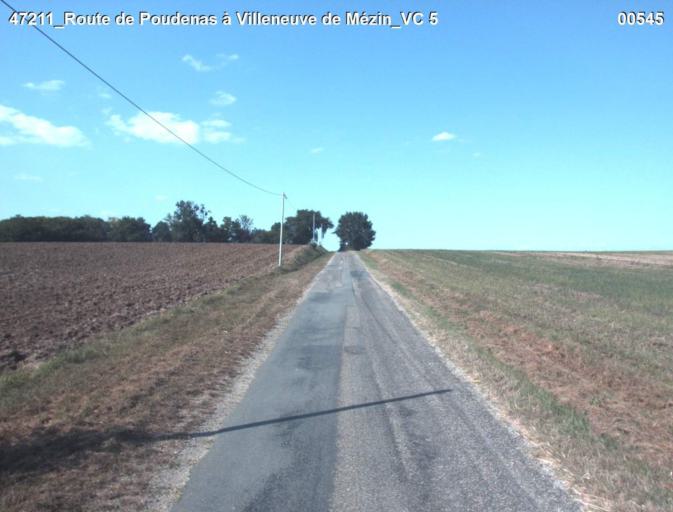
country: FR
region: Aquitaine
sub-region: Departement du Lot-et-Garonne
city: Mezin
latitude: 44.0388
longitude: 0.2191
